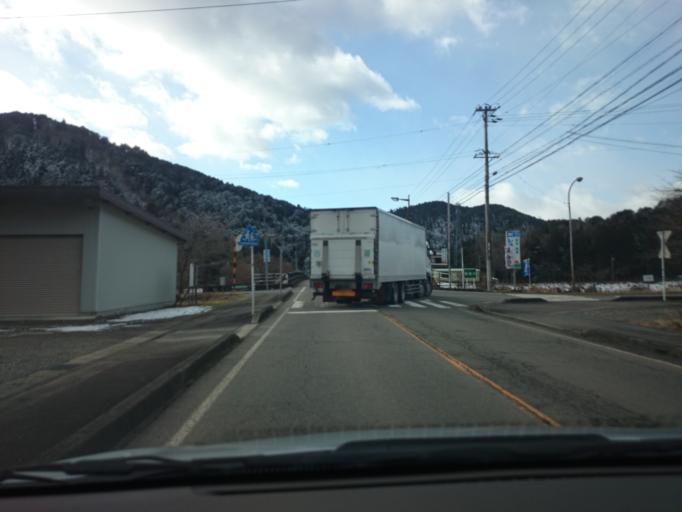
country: JP
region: Gifu
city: Gujo
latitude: 35.7411
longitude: 137.0723
